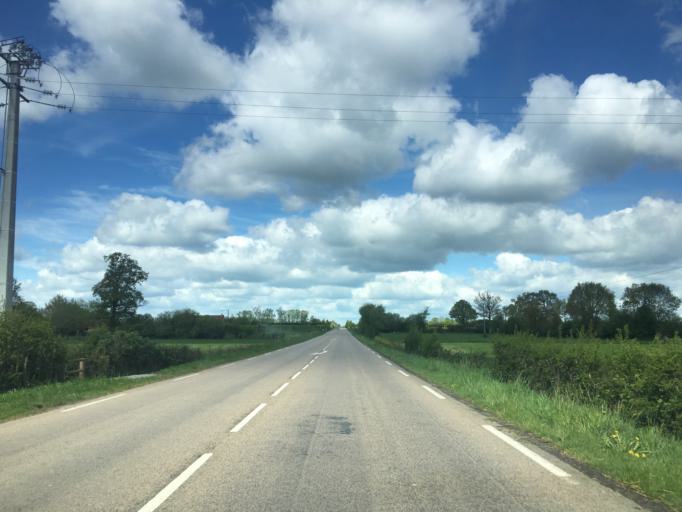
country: FR
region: Lower Normandy
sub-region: Departement de l'Orne
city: Rai
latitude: 48.8327
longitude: 0.5418
